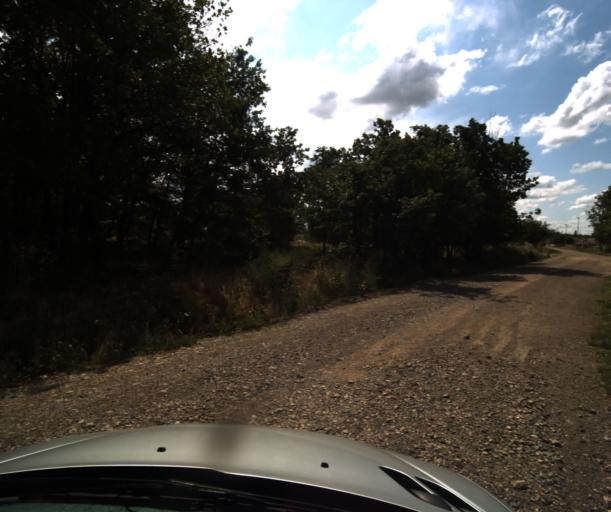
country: FR
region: Midi-Pyrenees
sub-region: Departement du Tarn-et-Garonne
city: Finhan
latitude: 43.9227
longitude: 1.2757
